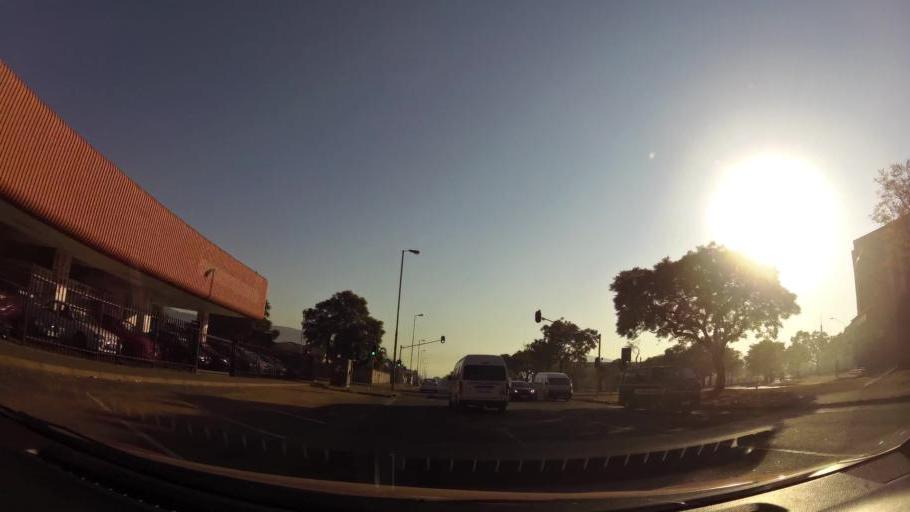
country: ZA
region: Gauteng
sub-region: City of Tshwane Metropolitan Municipality
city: Pretoria
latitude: -25.7130
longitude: 28.1844
